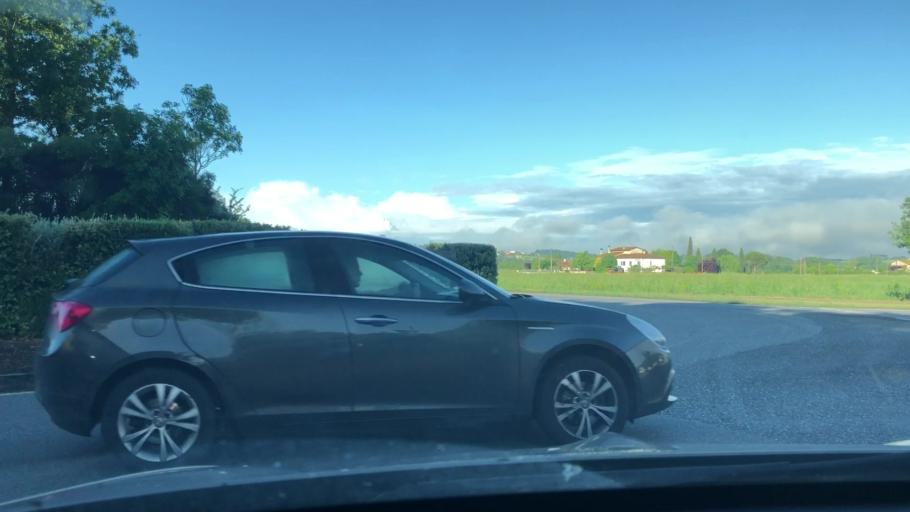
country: IT
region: Tuscany
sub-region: Province of Pisa
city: Forcoli
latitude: 43.6007
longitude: 10.6949
